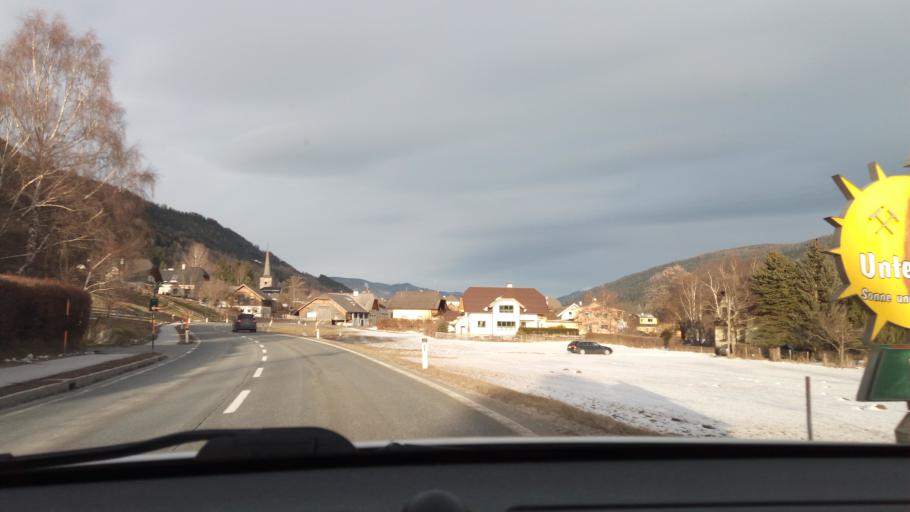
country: AT
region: Salzburg
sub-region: Politischer Bezirk Tamsweg
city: Mariapfarr
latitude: 47.1115
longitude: 13.7368
